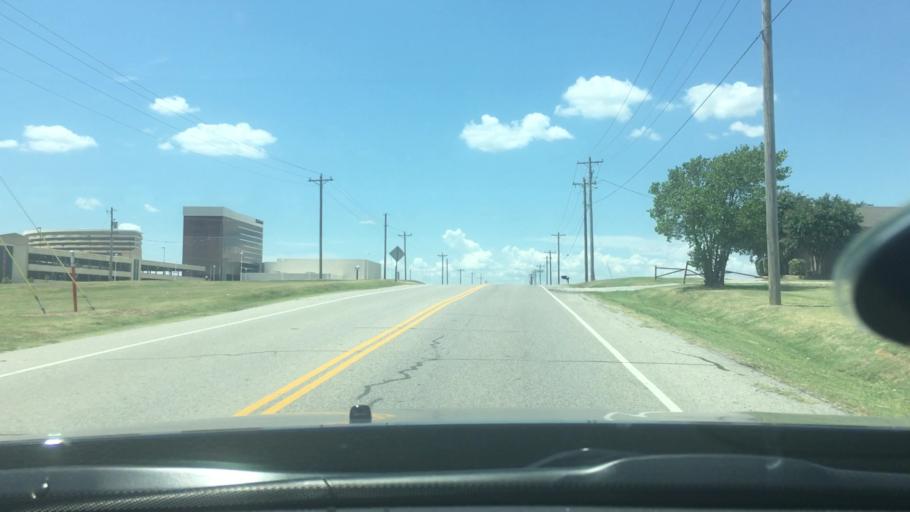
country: US
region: Oklahoma
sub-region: Bryan County
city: Calera
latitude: 33.9542
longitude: -96.4079
